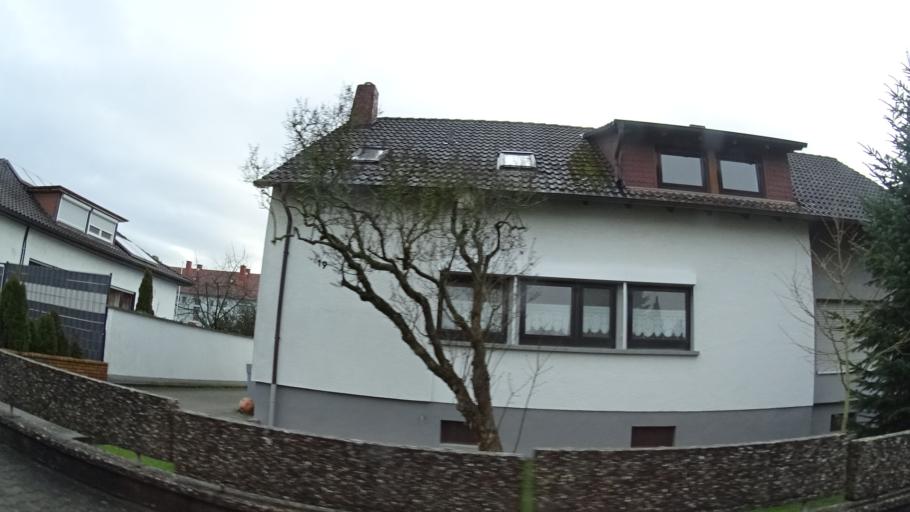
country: DE
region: Baden-Wuerttemberg
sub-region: Karlsruhe Region
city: Philippsburg
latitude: 49.2294
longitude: 8.4127
